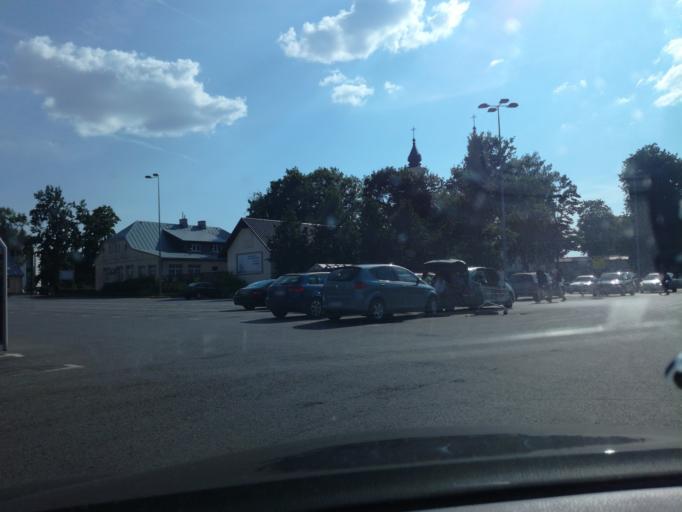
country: LT
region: Marijampoles apskritis
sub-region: Marijampole Municipality
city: Marijampole
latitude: 54.5559
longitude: 23.3466
